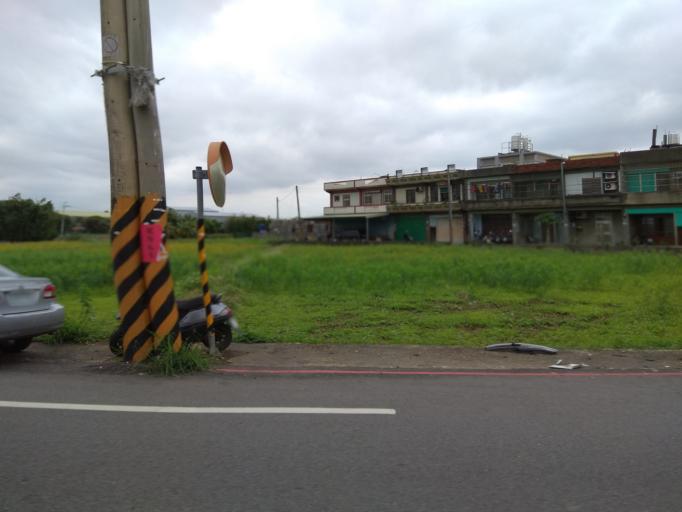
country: TW
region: Taiwan
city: Taoyuan City
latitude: 25.0482
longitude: 121.2232
